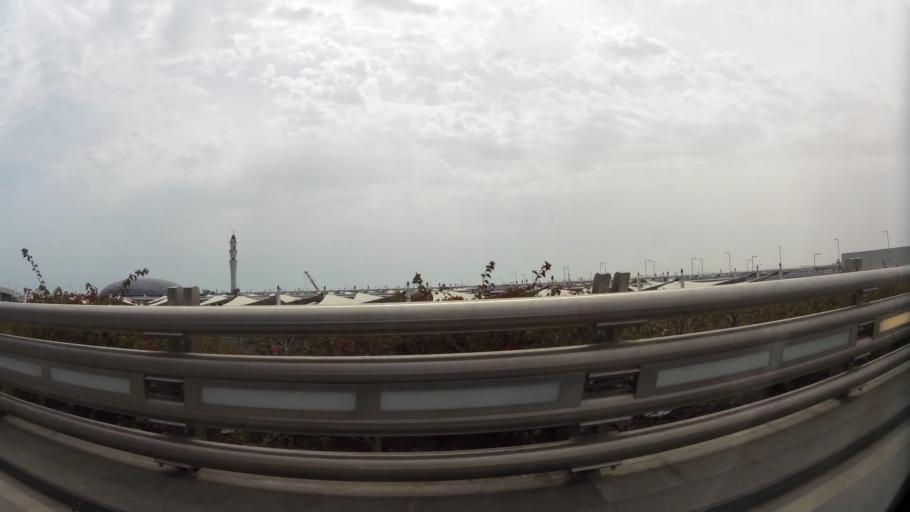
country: QA
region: Al Wakrah
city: Al Wakrah
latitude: 25.2589
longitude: 51.6129
